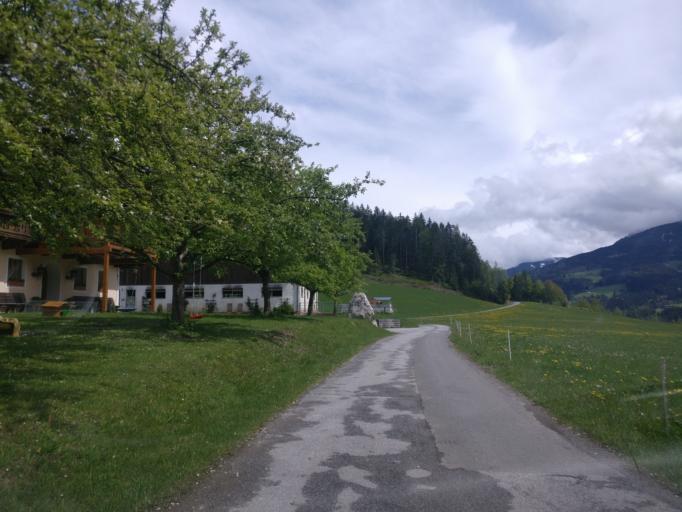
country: AT
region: Salzburg
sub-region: Politischer Bezirk Sankt Johann im Pongau
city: Bischofshofen
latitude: 47.4400
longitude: 13.2265
